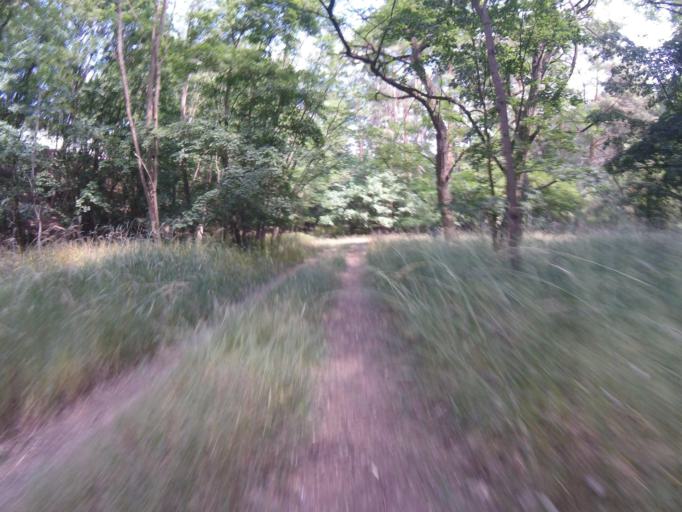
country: DE
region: Brandenburg
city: Wildau
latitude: 52.3097
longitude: 13.6276
